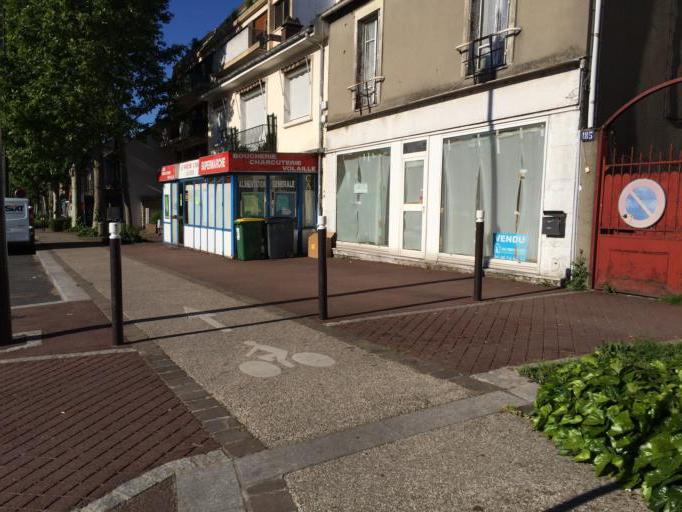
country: FR
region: Ile-de-France
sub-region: Departement des Hauts-de-Seine
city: Antony
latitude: 48.7396
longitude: 2.3023
